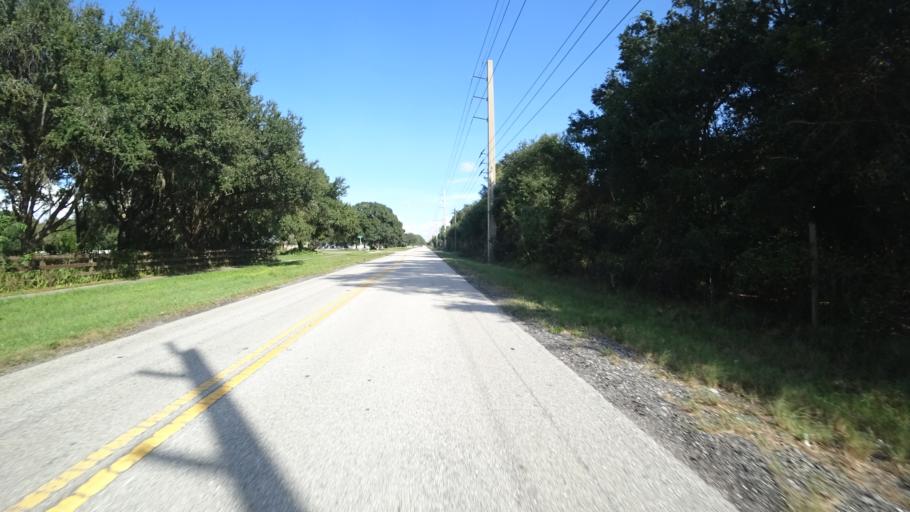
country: US
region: Florida
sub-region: Manatee County
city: Samoset
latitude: 27.4617
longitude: -82.4839
